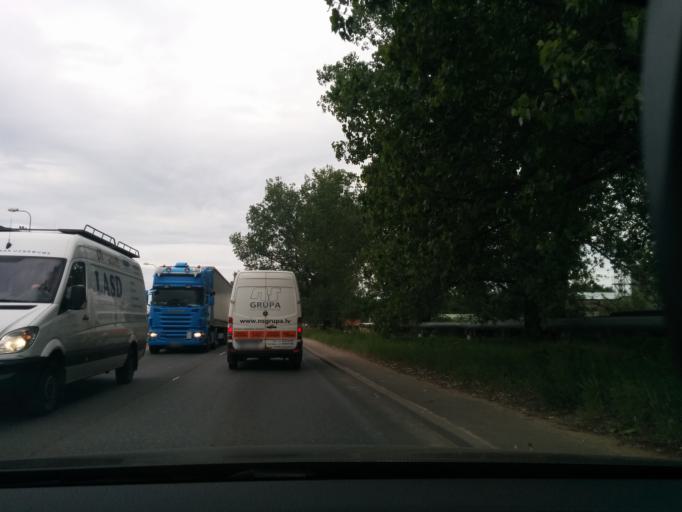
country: LV
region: Kekava
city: Kekava
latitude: 56.9127
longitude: 24.2042
